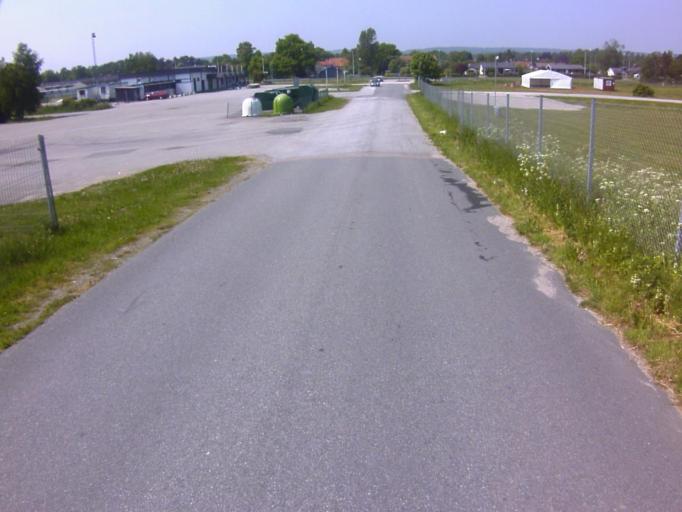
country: SE
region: Blekinge
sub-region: Karlshamns Kommun
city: Morrum
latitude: 56.1174
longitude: 14.6795
